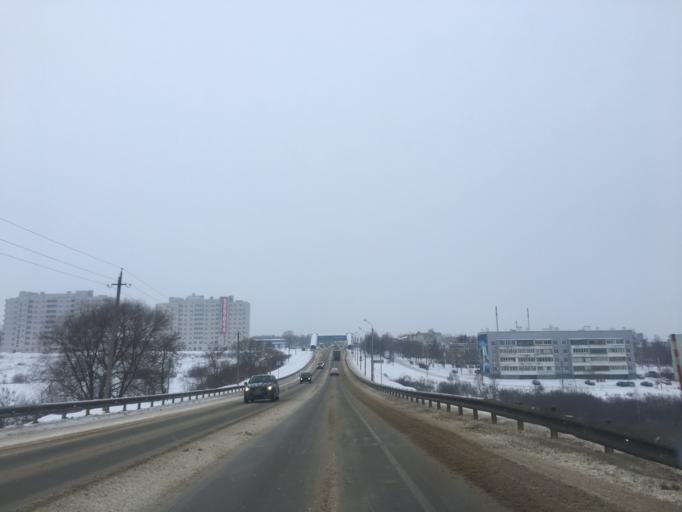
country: RU
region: Tula
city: Kosaya Gora
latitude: 54.1610
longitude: 37.4749
